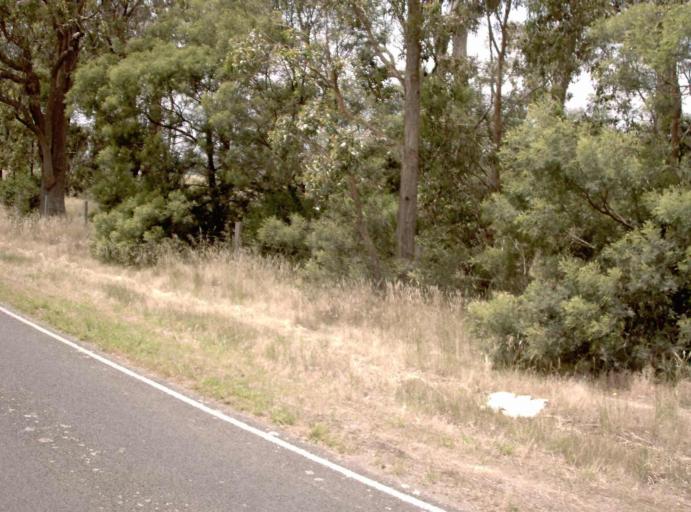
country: AU
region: Victoria
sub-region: Latrobe
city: Traralgon
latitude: -38.5387
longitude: 146.6571
